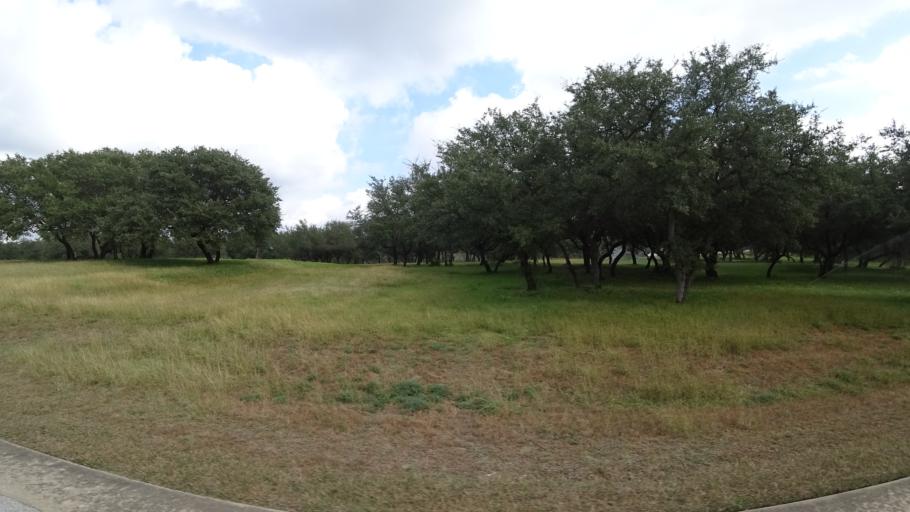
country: US
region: Texas
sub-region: Travis County
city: Barton Creek
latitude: 30.3050
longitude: -97.8934
